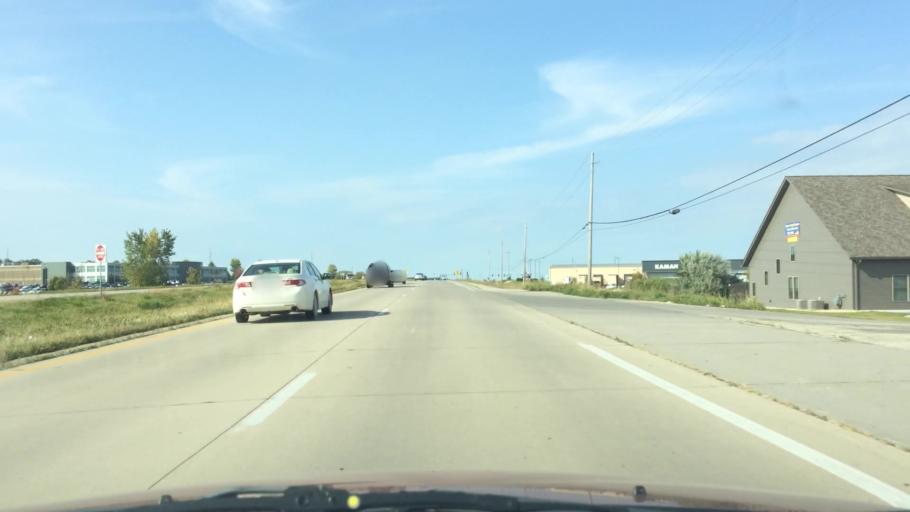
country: US
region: Minnesota
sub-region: Olmsted County
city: Rochester
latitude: 44.0533
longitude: -92.5229
